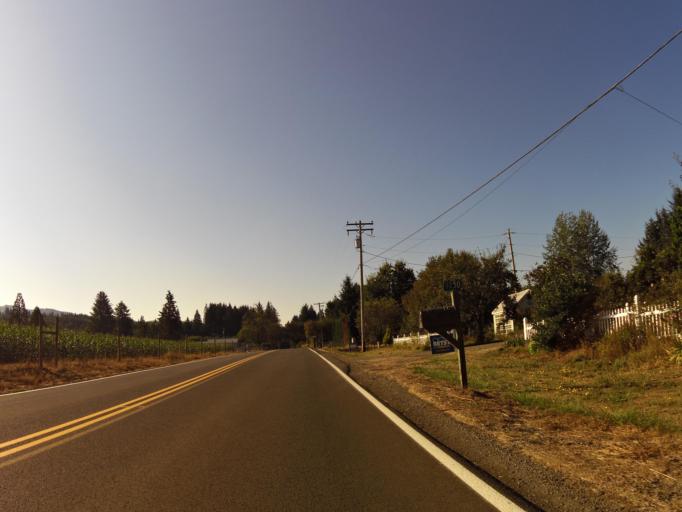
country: US
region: Oregon
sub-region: Tillamook County
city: Tillamook
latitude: 45.3889
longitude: -123.7945
